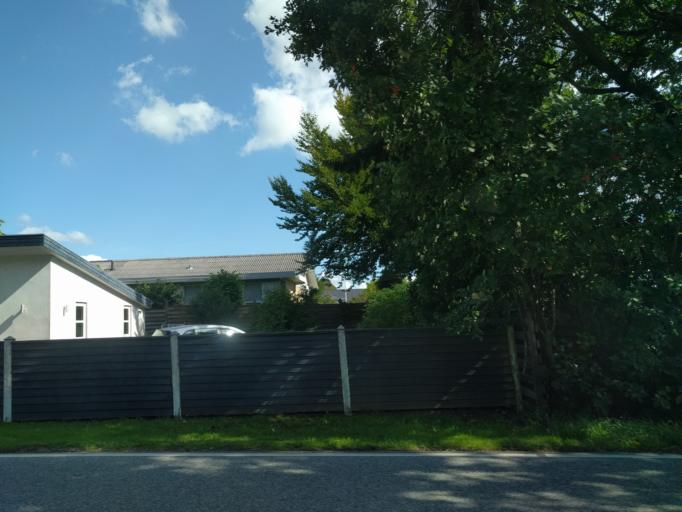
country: DK
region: Central Jutland
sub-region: Skive Kommune
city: Skive
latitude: 56.5868
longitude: 9.0294
